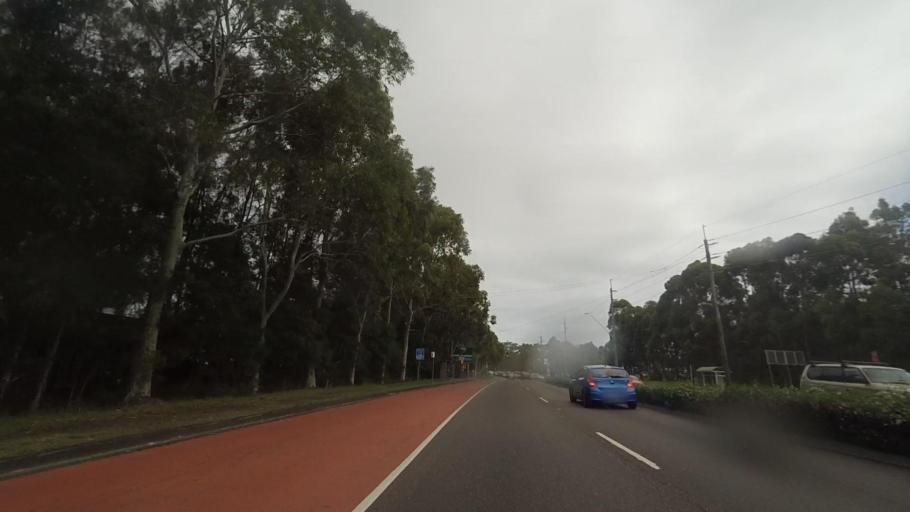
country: AU
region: New South Wales
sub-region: Wyong Shire
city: Tumbi Vmbi
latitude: -33.3607
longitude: 151.4428
